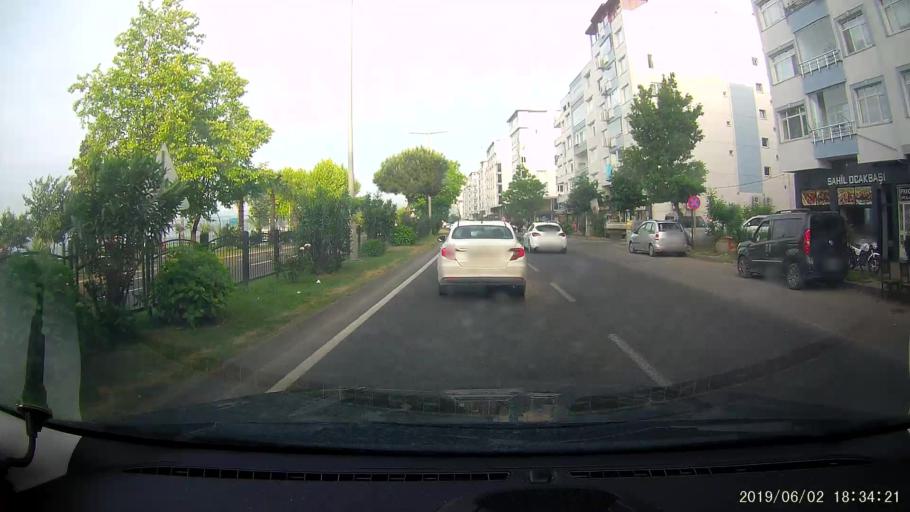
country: TR
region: Ordu
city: Fatsa
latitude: 41.0298
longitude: 37.5033
